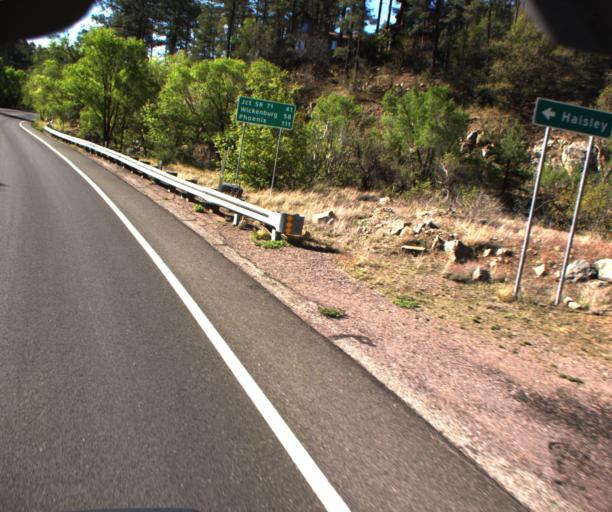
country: US
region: Arizona
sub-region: Yavapai County
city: Prescott
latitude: 34.5187
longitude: -112.4787
